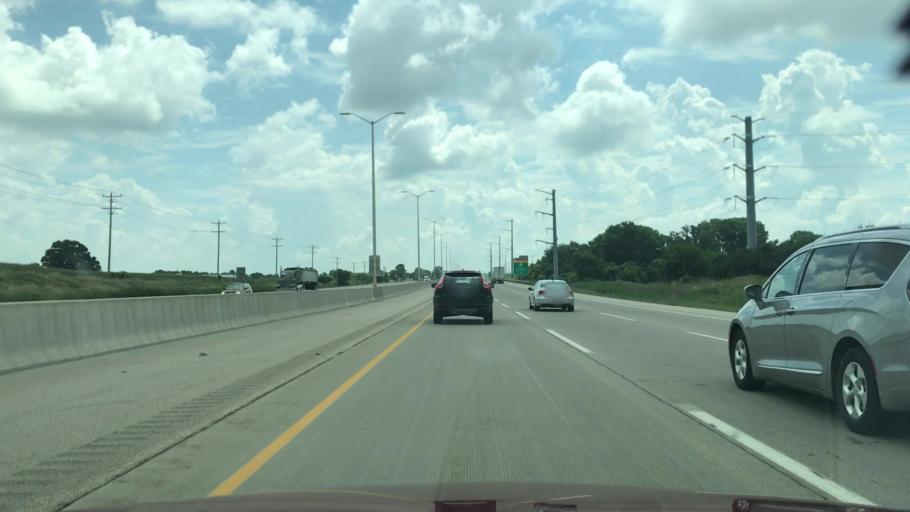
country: US
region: Illinois
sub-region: McHenry County
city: Huntley
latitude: 42.1299
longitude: -88.4560
